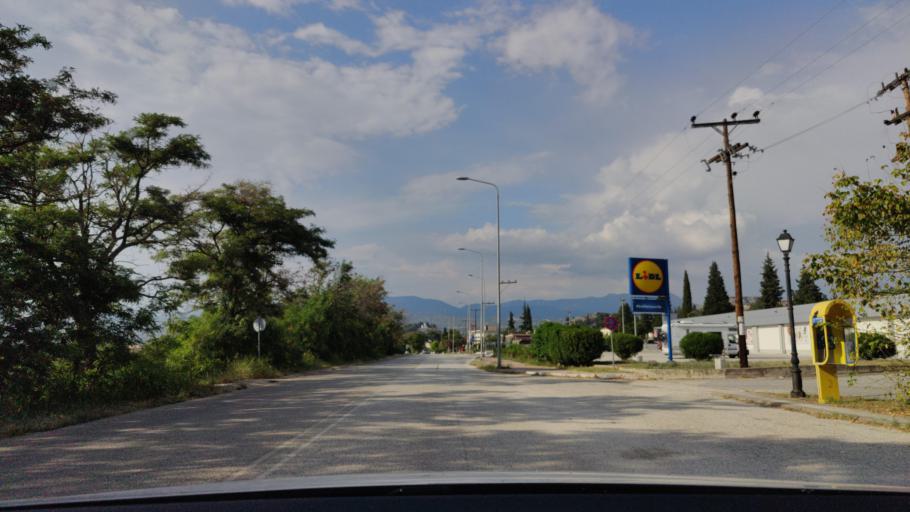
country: GR
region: Central Macedonia
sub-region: Nomos Serron
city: Sidirokastro
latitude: 41.2274
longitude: 23.3909
